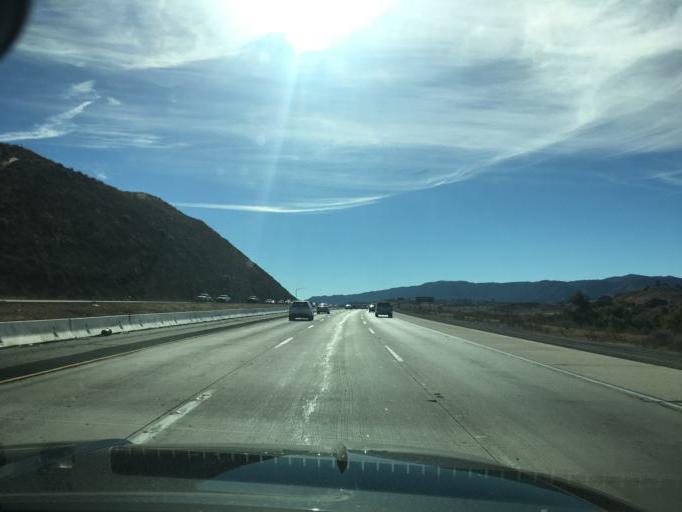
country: US
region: California
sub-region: Riverside County
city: Lake Elsinore
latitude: 33.7150
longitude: -117.3615
